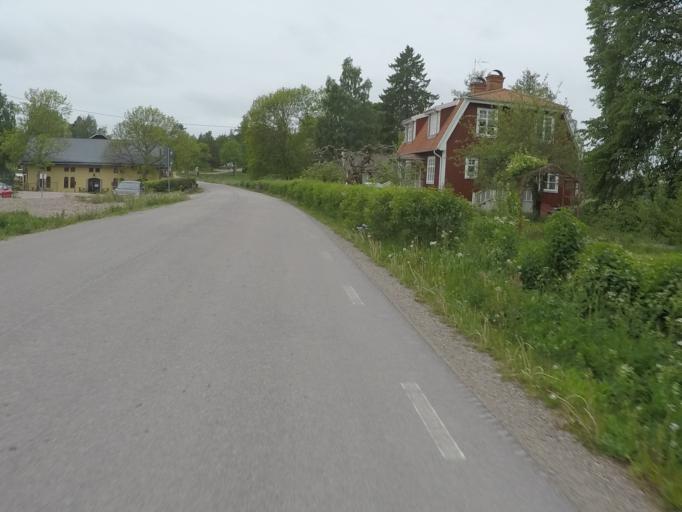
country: SE
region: Vaestmanland
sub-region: Hallstahammars Kommun
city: Kolback
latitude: 59.5462
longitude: 16.2528
